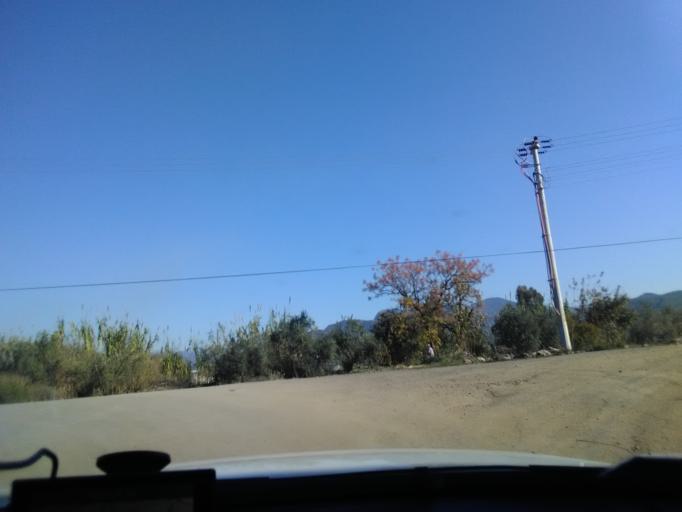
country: TR
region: Antalya
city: Gazipasa
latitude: 36.2498
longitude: 32.3408
